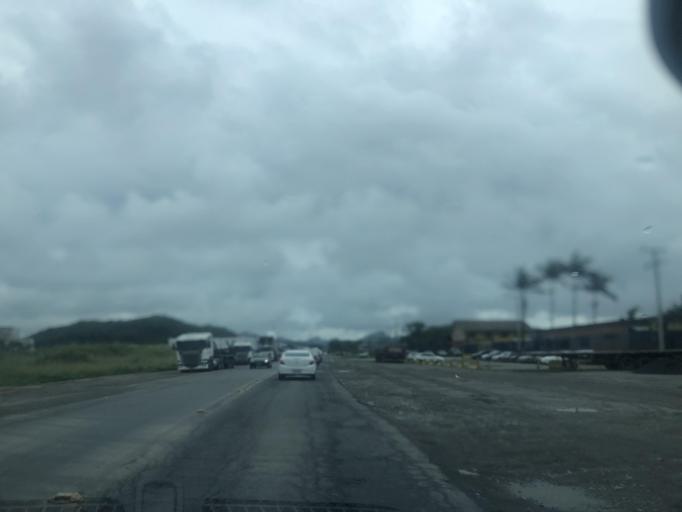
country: BR
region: Santa Catarina
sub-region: Sao Francisco Do Sul
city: Sao Francisco do Sul
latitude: -26.2501
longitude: -48.6164
